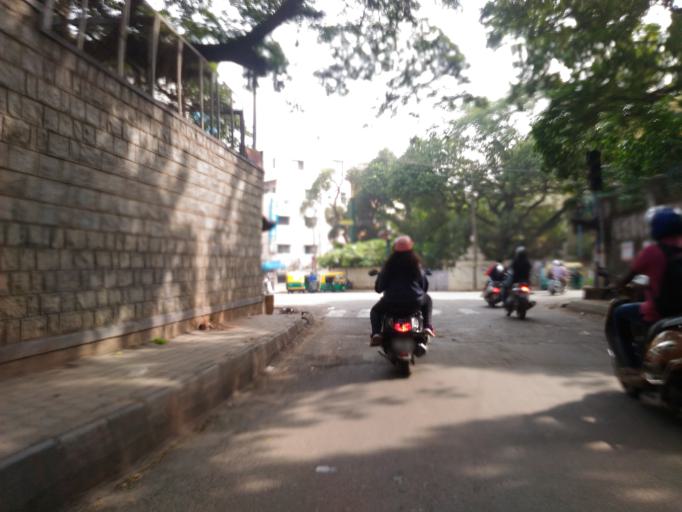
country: IN
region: Karnataka
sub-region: Bangalore Urban
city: Bangalore
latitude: 12.9650
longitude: 77.6096
